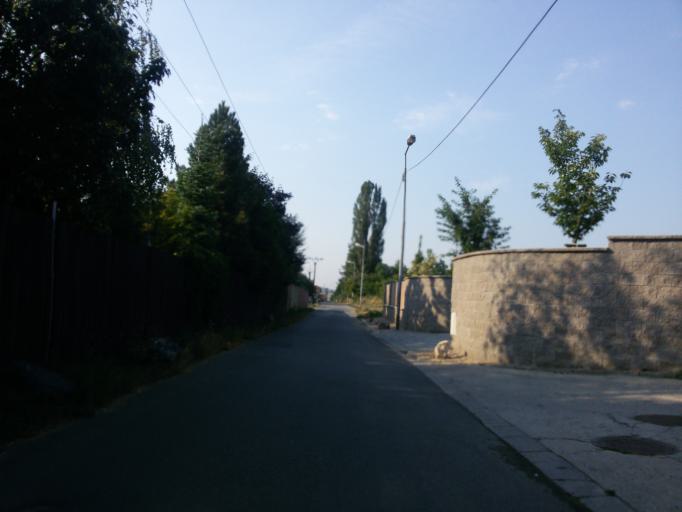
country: CZ
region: South Moravian
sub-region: Okres Brno-Venkov
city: Lelekovice
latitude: 49.2696
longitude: 16.5668
